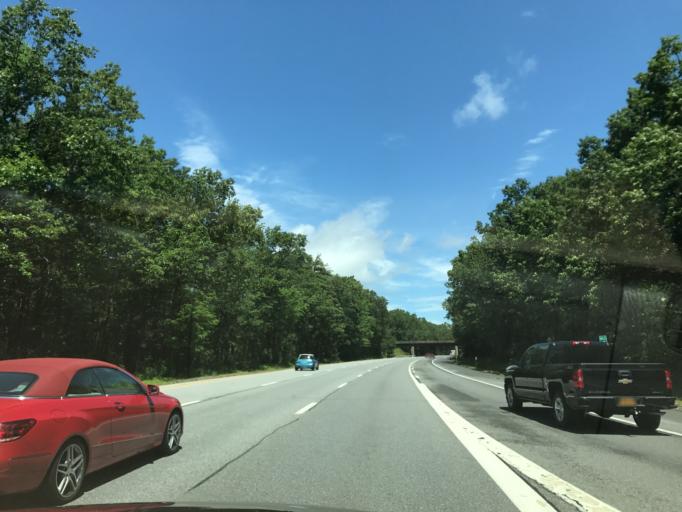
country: US
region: New York
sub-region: Warren County
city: West Glens Falls
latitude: 43.2398
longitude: -73.6920
